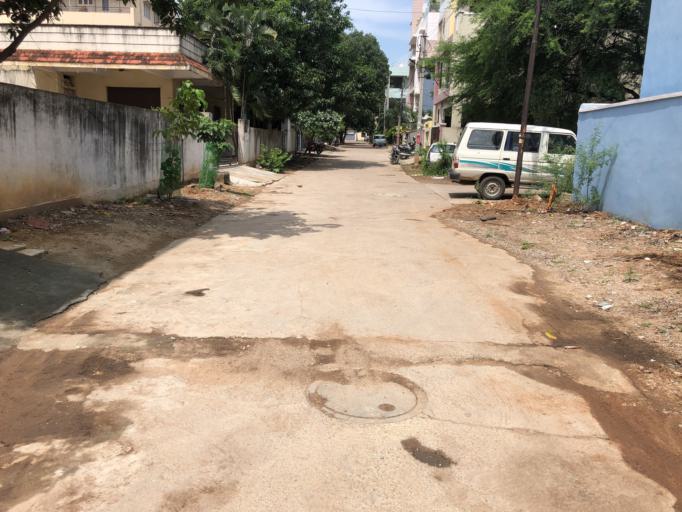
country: IN
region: Telangana
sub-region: Rangareddi
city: Quthbullapur
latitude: 17.4853
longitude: 78.4810
